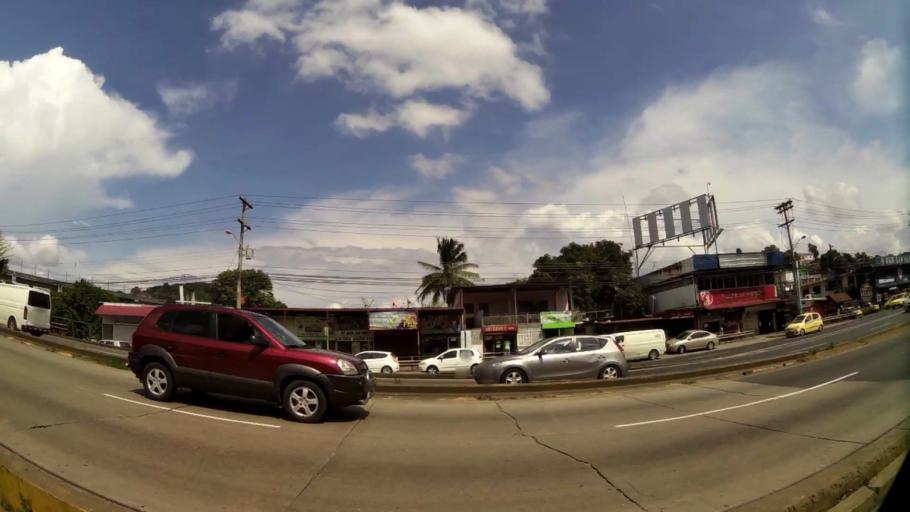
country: PA
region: Panama
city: San Miguelito
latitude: 9.0306
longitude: -79.5045
